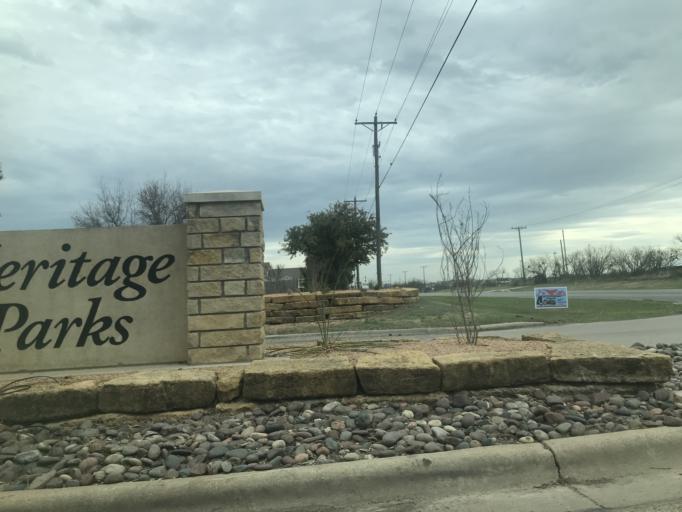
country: US
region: Texas
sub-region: Taylor County
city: Abilene
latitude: 32.4874
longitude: -99.6904
